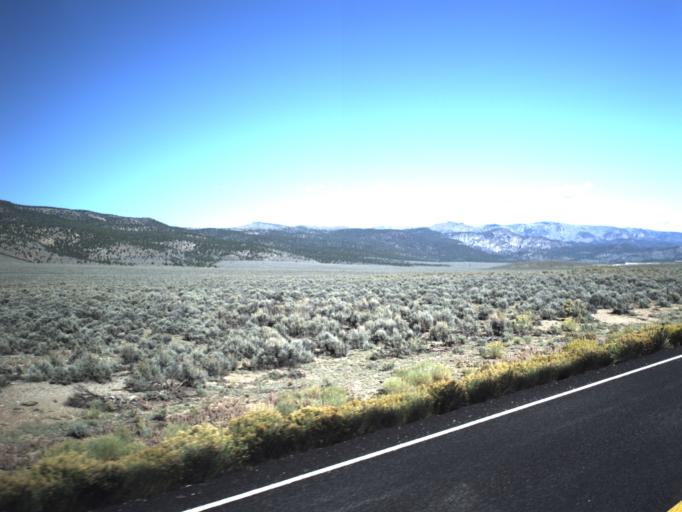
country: US
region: Utah
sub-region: Piute County
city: Junction
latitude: 38.2283
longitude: -111.9964
